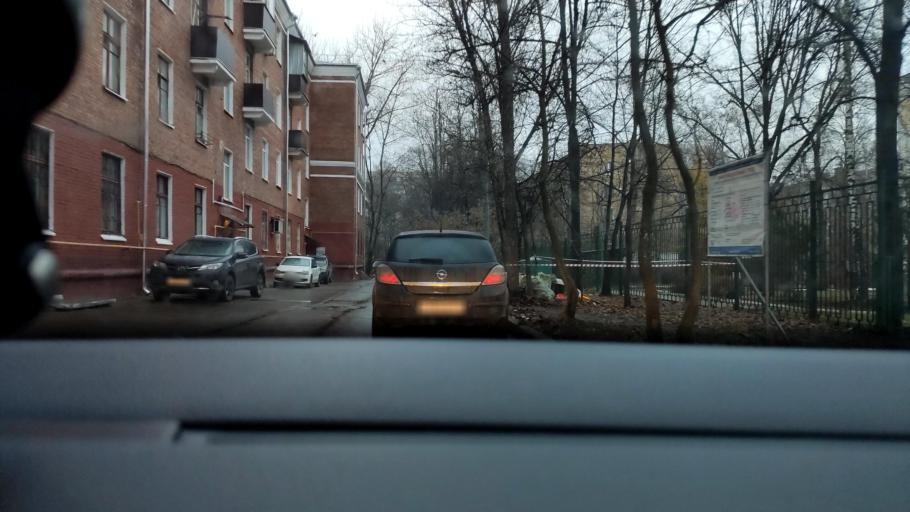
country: RU
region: Moscow
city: Metrogorodok
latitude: 55.8136
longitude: 37.7896
